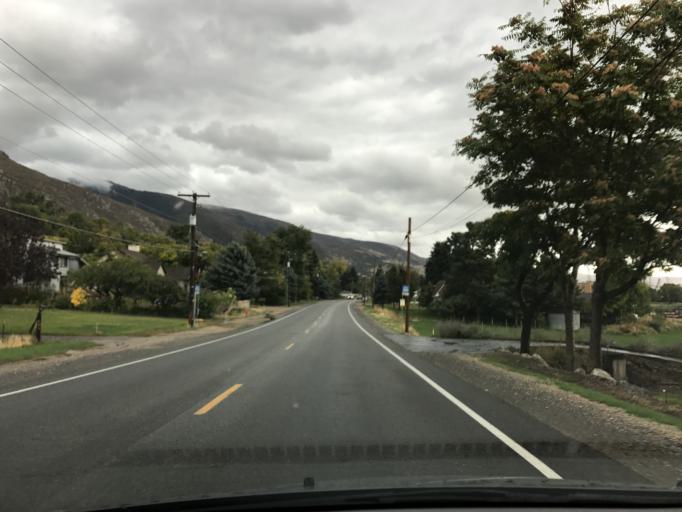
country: US
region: Utah
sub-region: Davis County
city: Farmington
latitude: 40.9958
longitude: -111.8968
